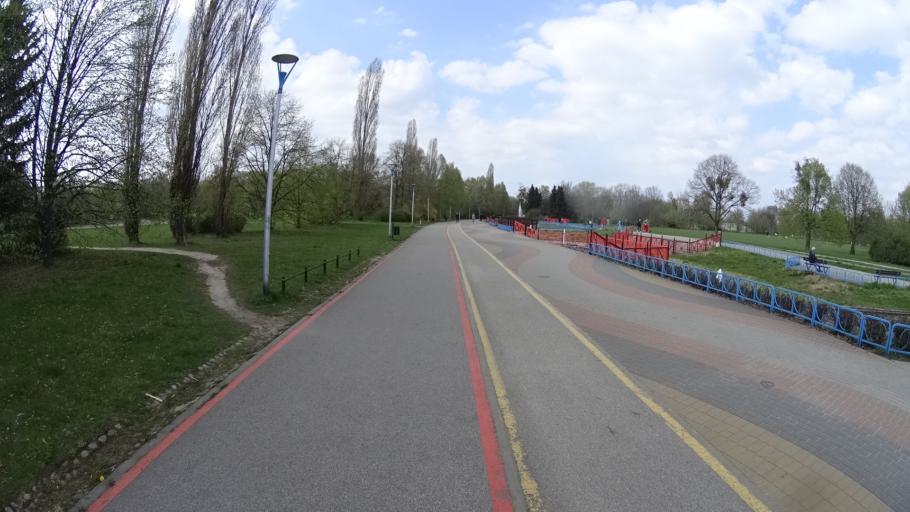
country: PL
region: Masovian Voivodeship
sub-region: Warszawa
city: Ochota
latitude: 52.2333
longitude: 20.9499
